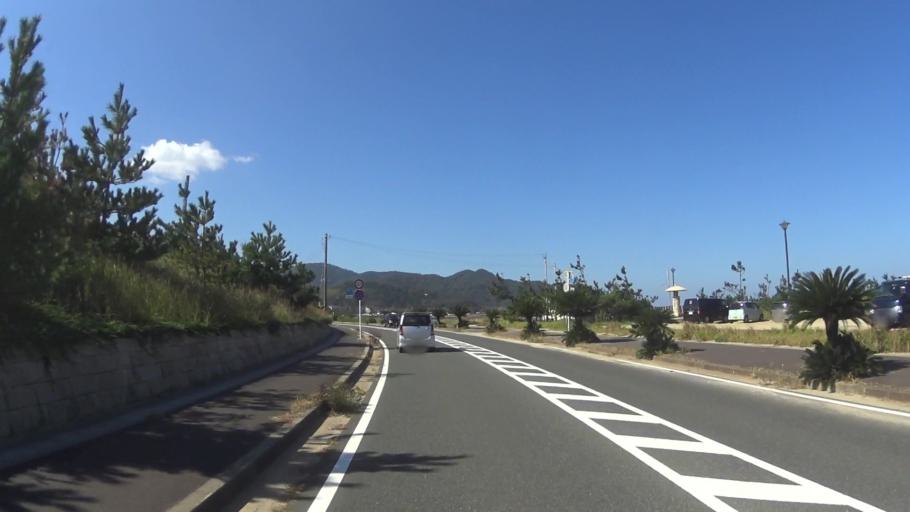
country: JP
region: Kyoto
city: Miyazu
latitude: 35.6906
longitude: 135.0298
